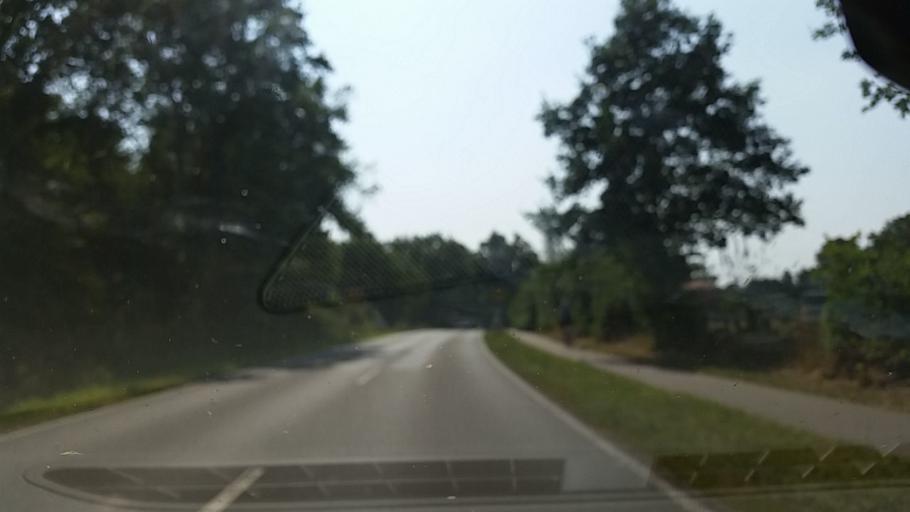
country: DE
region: Schleswig-Holstein
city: Witzhave
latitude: 53.5682
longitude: 10.3417
